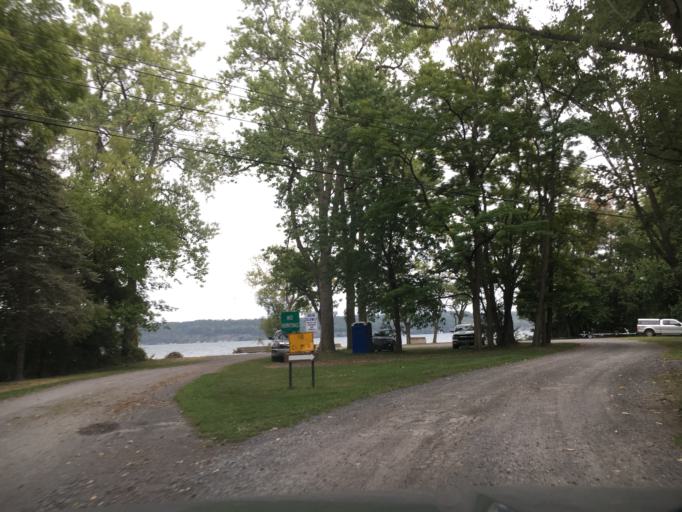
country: US
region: New York
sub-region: Tompkins County
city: Trumansburg
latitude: 42.6656
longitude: -76.7002
